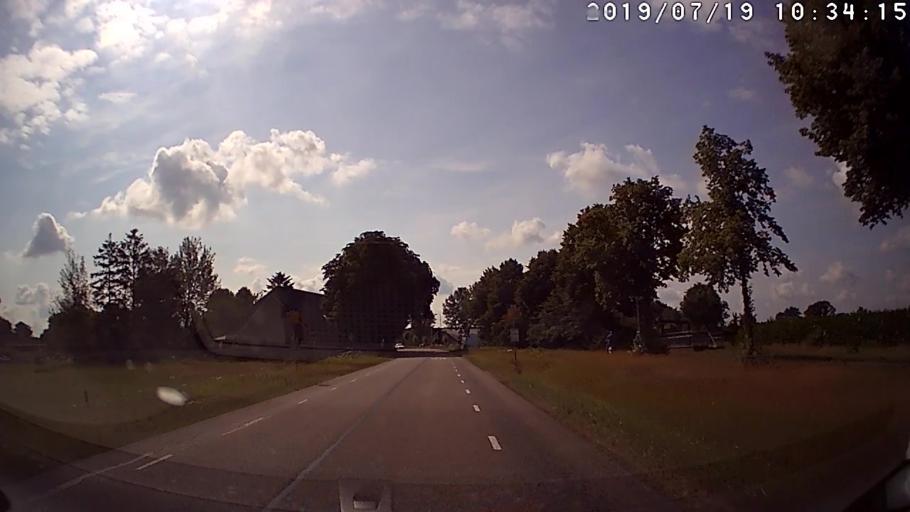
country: NL
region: Drenthe
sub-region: Gemeente Hoogeveen
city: Hoogeveen
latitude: 52.5992
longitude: 6.4199
